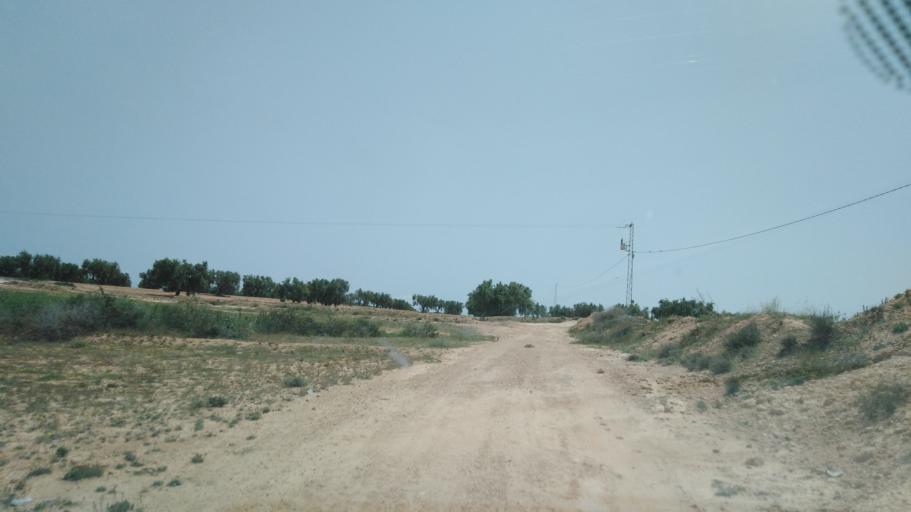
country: TN
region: Safaqis
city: Sfax
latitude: 34.7204
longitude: 10.5699
